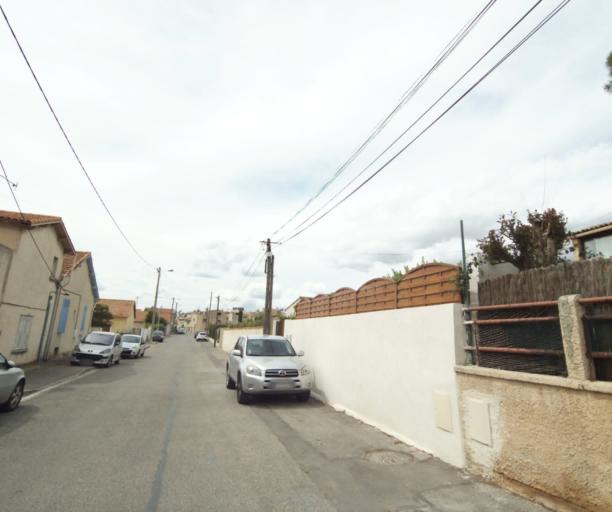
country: FR
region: Provence-Alpes-Cote d'Azur
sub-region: Departement des Bouches-du-Rhone
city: Rognac
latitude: 43.4871
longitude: 5.2364
